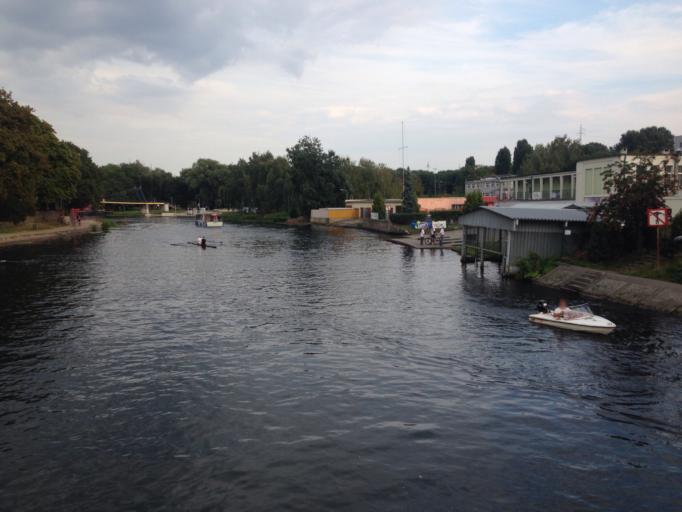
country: PL
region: Kujawsko-Pomorskie
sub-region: Bydgoszcz
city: Bydgoszcz
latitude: 53.1210
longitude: 18.0194
